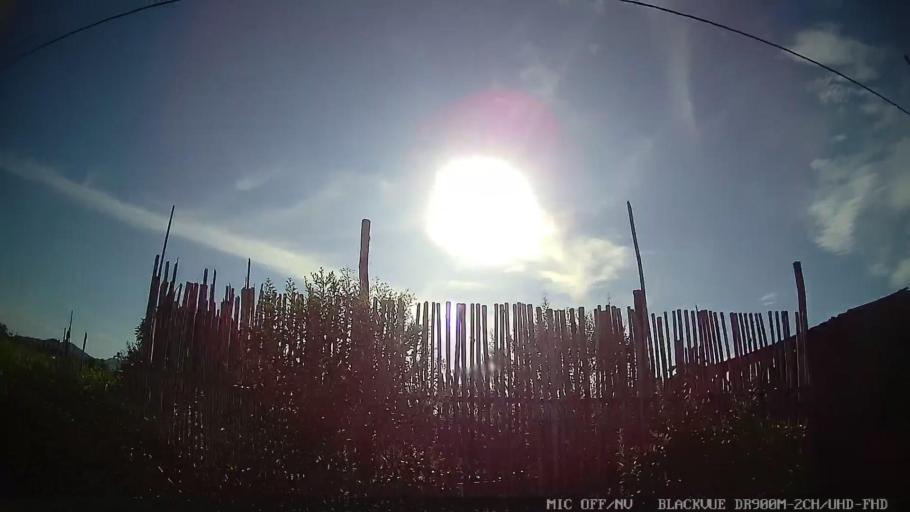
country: BR
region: Sao Paulo
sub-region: Iguape
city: Iguape
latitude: -24.7568
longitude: -47.5769
